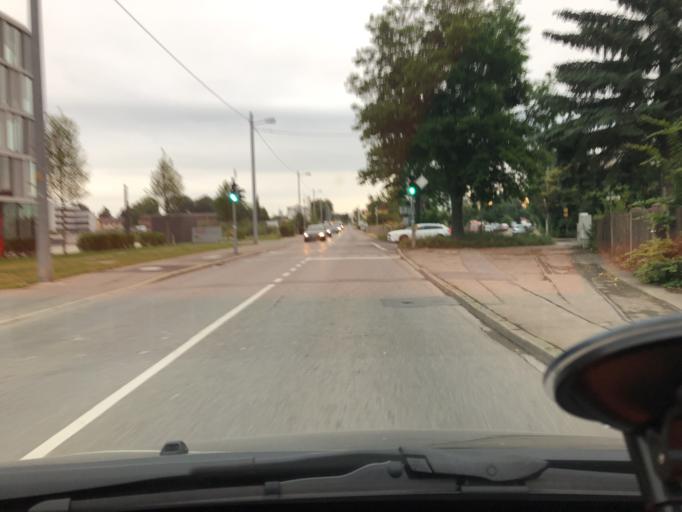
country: DE
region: Baden-Wuerttemberg
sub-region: Regierungsbezirk Stuttgart
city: Leinfelden-Echterdingen
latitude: 48.7302
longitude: 9.1548
